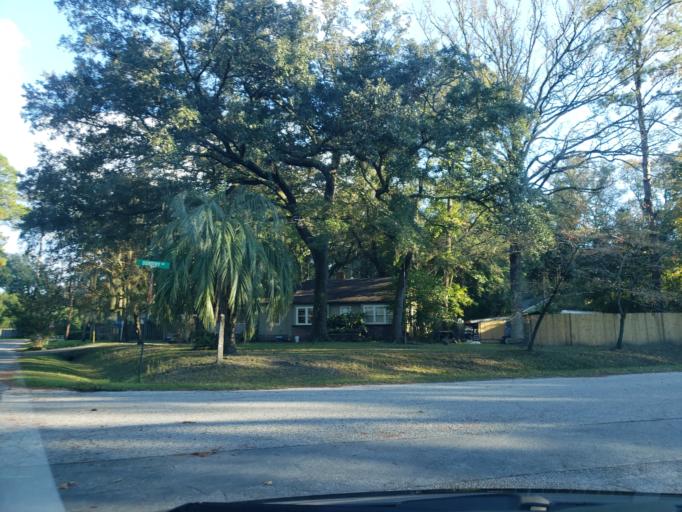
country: US
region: Georgia
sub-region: Chatham County
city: Isle of Hope
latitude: 31.9763
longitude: -81.0588
